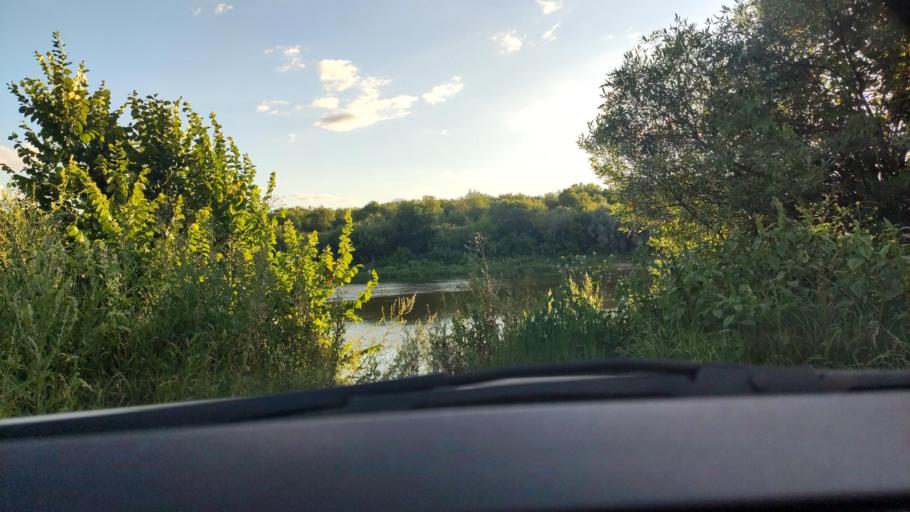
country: RU
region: Voronezj
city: Semiluki
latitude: 51.6816
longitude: 39.0475
